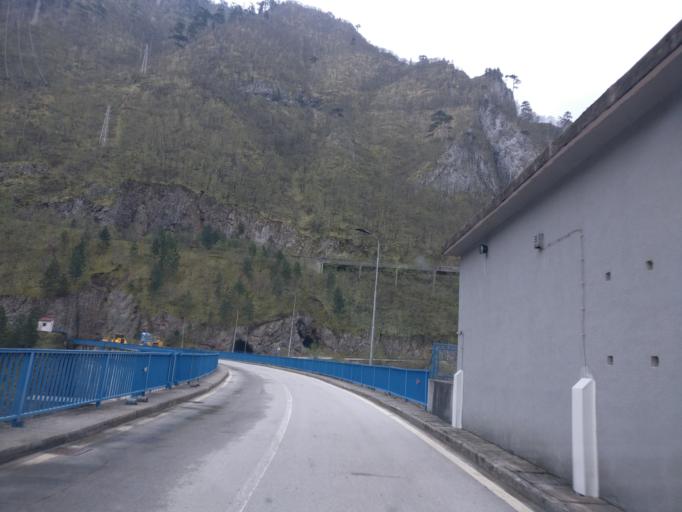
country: ME
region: Opstina Pluzine
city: Pluzine
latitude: 43.2727
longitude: 18.8423
